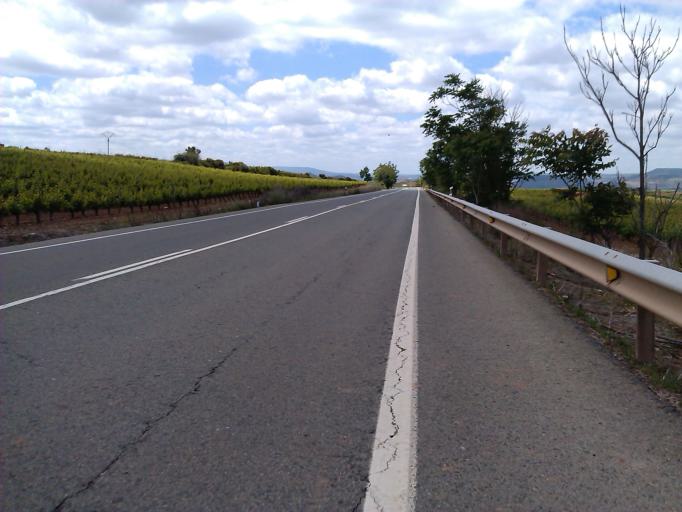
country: ES
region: La Rioja
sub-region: Provincia de La Rioja
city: Manjarres
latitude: 42.4108
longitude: -2.6564
